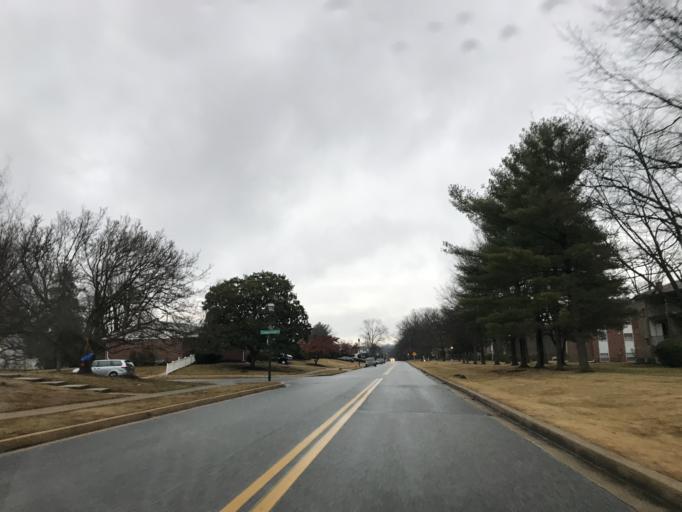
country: US
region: Maryland
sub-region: Baltimore County
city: Pikesville
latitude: 39.3720
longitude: -76.6885
